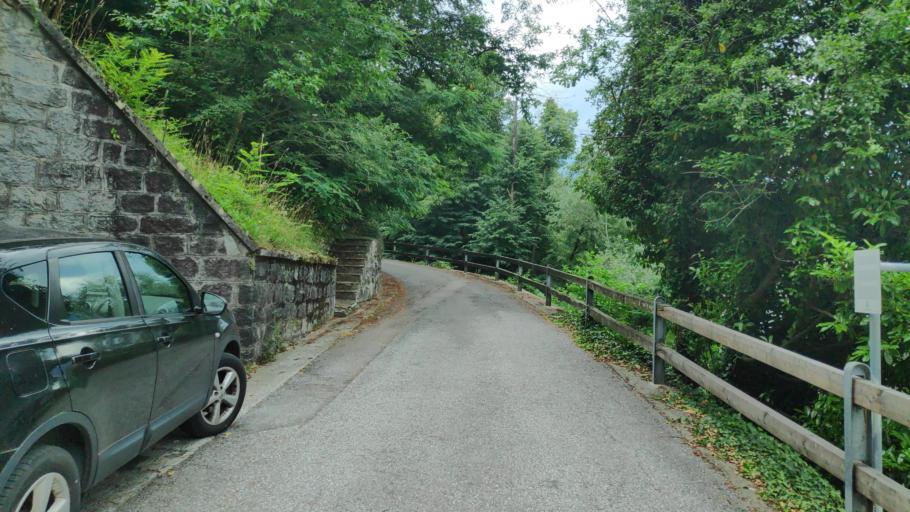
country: IT
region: Lombardy
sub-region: Provincia di Sondrio
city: Prata Camportaccio
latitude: 46.3017
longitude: 9.3987
